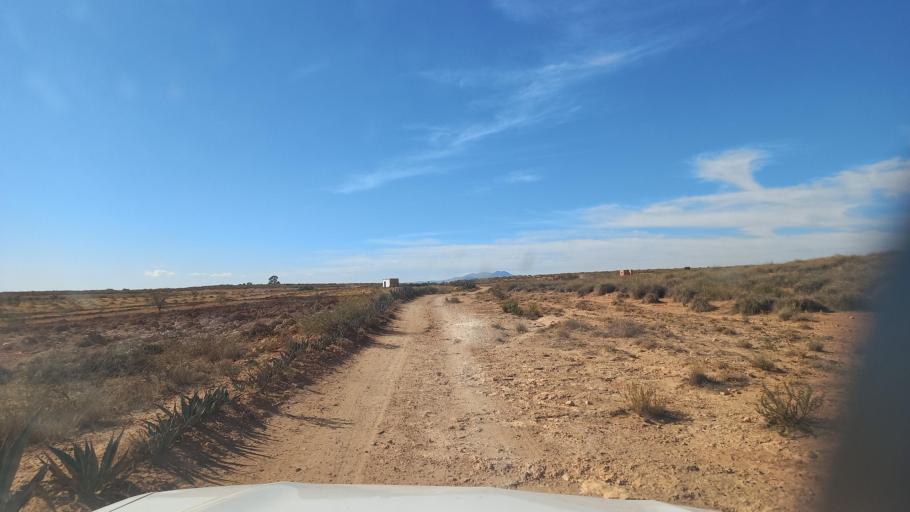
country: TN
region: Al Qasrayn
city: Kasserine
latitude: 35.2147
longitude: 8.9792
